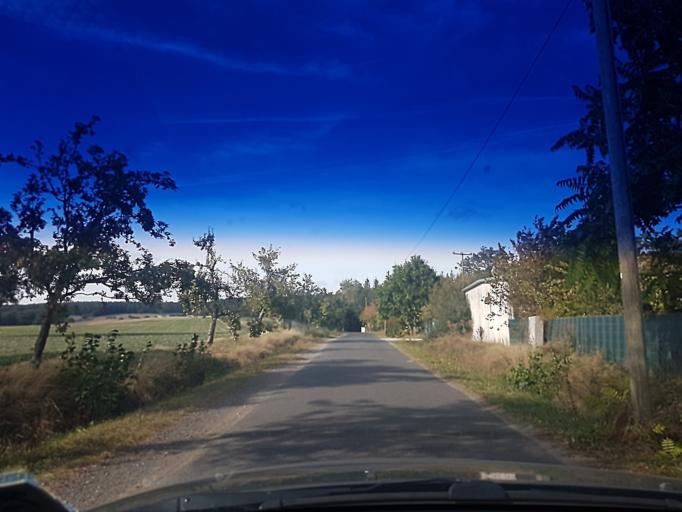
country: DE
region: Bavaria
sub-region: Upper Franconia
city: Burgwindheim
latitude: 49.7777
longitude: 10.5441
